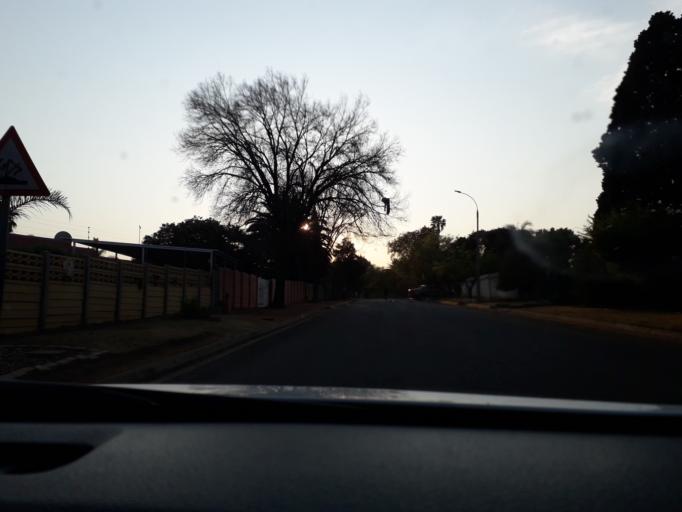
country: ZA
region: Gauteng
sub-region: City of Johannesburg Metropolitan Municipality
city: Modderfontein
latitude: -26.0631
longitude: 28.2041
